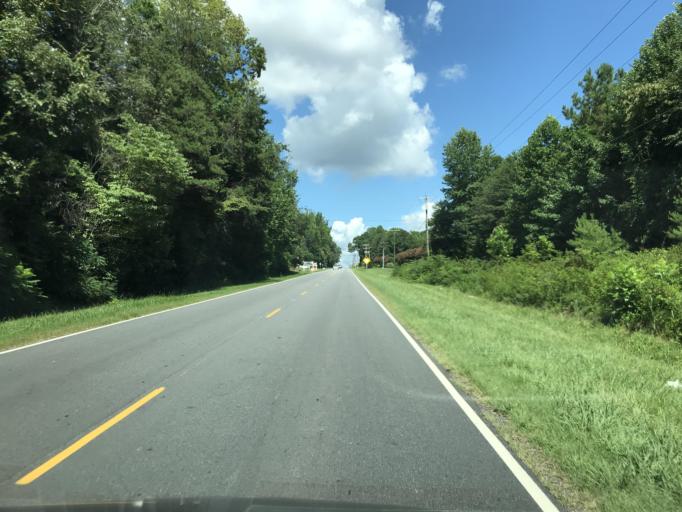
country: US
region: North Carolina
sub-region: Catawba County
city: Lake Norman of Catawba
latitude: 35.5795
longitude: -80.9977
